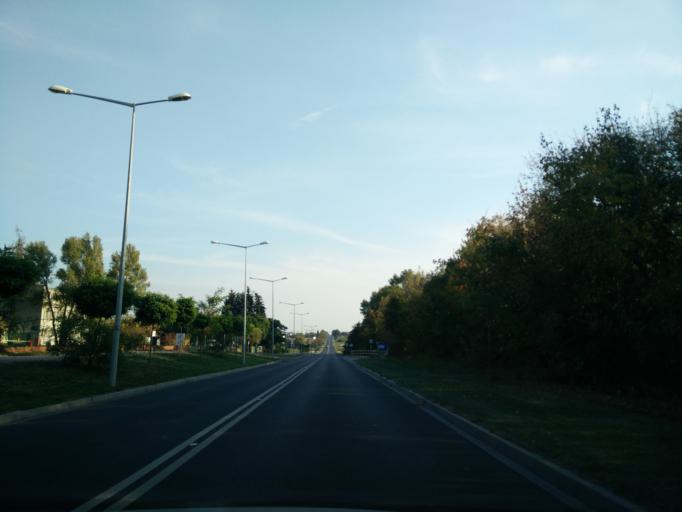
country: PL
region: Greater Poland Voivodeship
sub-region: Powiat sredzki
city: Sroda Wielkopolska
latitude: 52.2167
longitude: 17.2920
